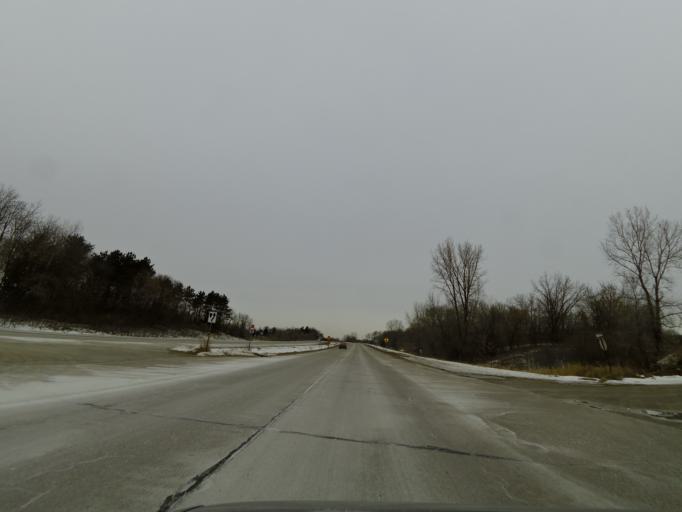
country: US
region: Minnesota
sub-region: Washington County
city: Lake Elmo
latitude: 44.9597
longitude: -92.9029
